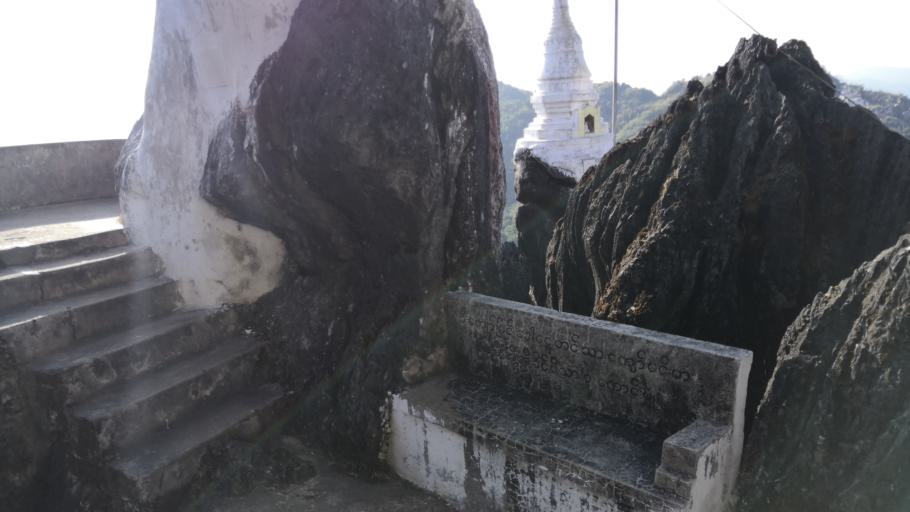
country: MM
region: Mandalay
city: Mogok
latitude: 22.9021
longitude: 96.3773
